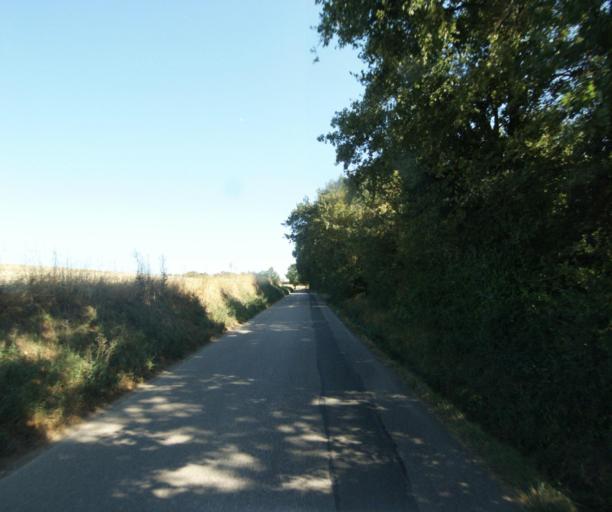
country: FR
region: Rhone-Alpes
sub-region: Departement du Rhone
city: Lentilly
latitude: 45.8159
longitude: 4.6731
